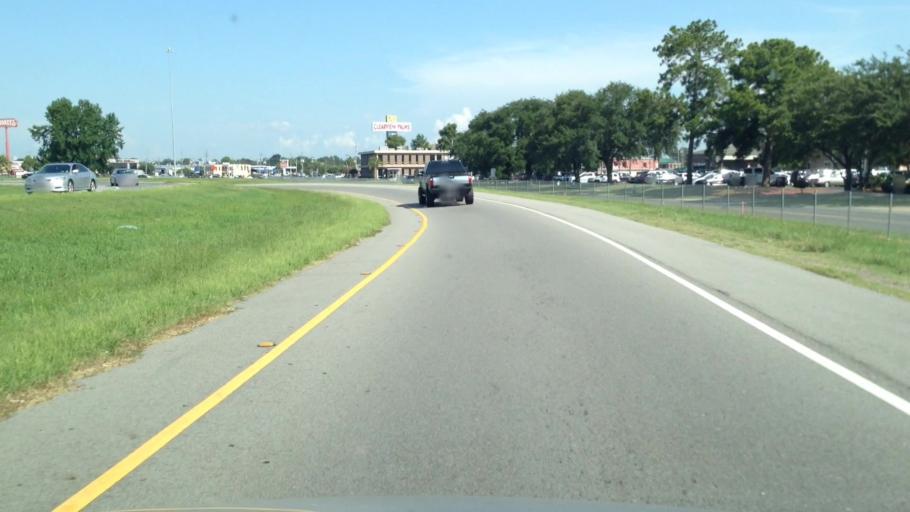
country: US
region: Louisiana
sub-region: Jefferson Parish
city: Metairie Terrace
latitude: 29.9978
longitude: -90.1863
